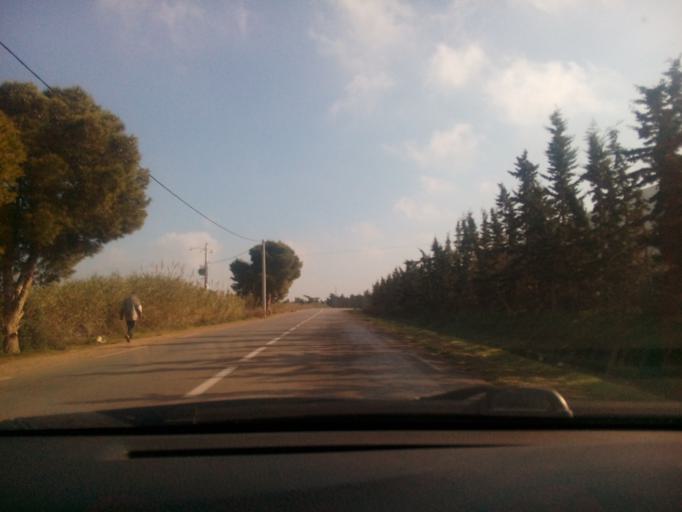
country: DZ
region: Oran
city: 'Ain el Turk
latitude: 35.7040
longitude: -0.8408
